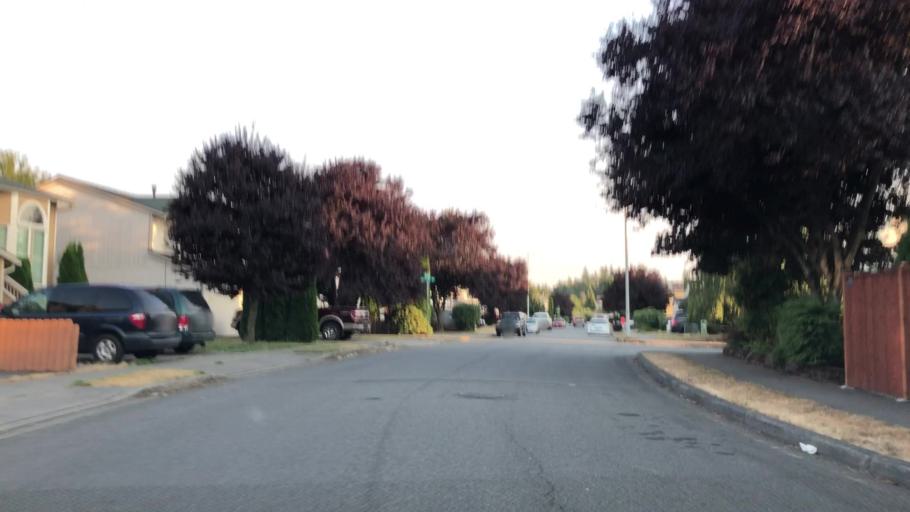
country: US
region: Washington
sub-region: Snohomish County
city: Marysville
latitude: 48.0914
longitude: -122.1530
